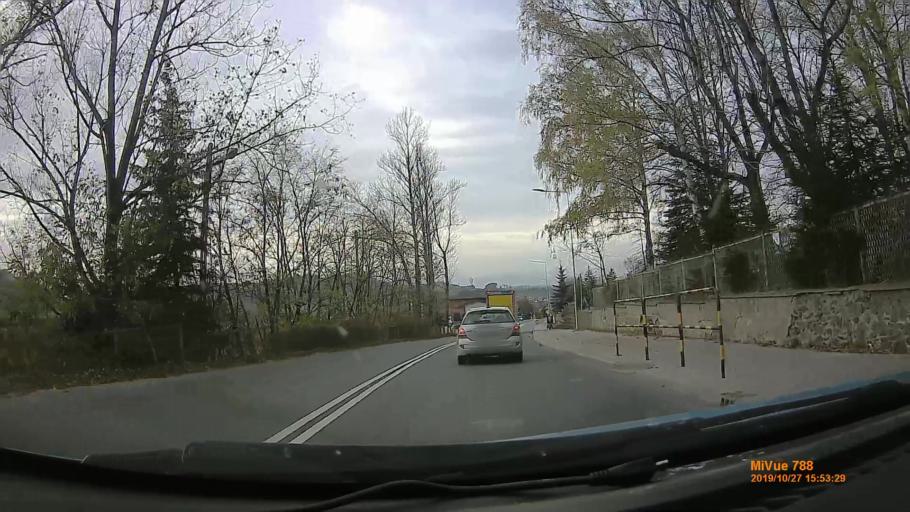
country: PL
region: Lower Silesian Voivodeship
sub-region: Powiat klodzki
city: Bozkow
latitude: 50.5376
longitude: 16.5659
